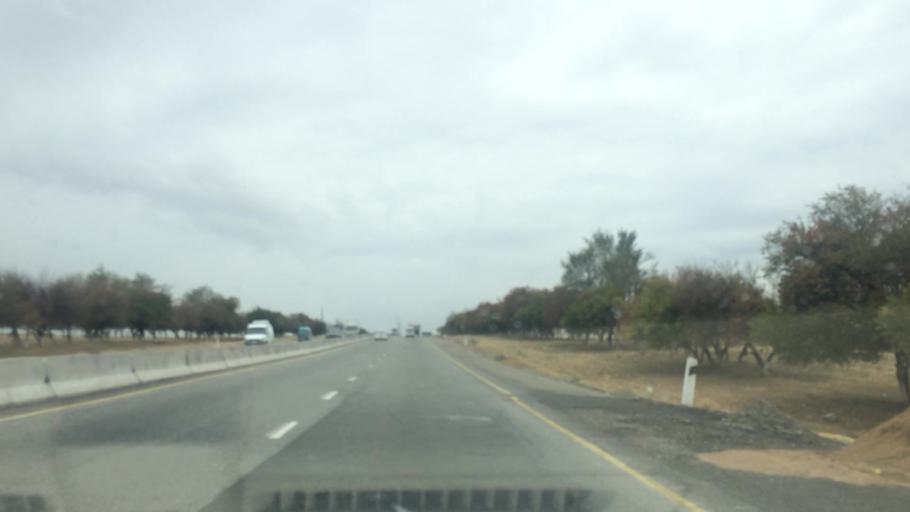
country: UZ
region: Samarqand
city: Bulung'ur
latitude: 39.8573
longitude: 67.4677
